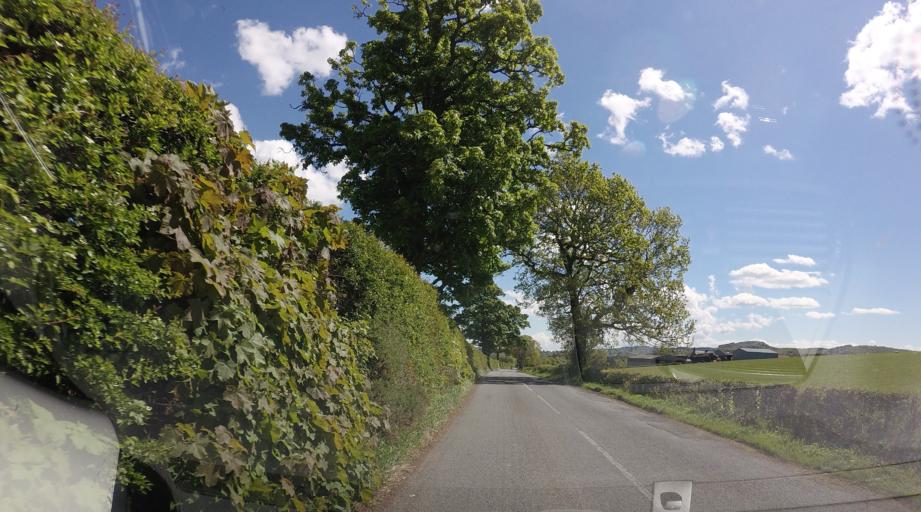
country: GB
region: Scotland
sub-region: Falkirk
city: Polmont
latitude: 55.9727
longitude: -3.6802
